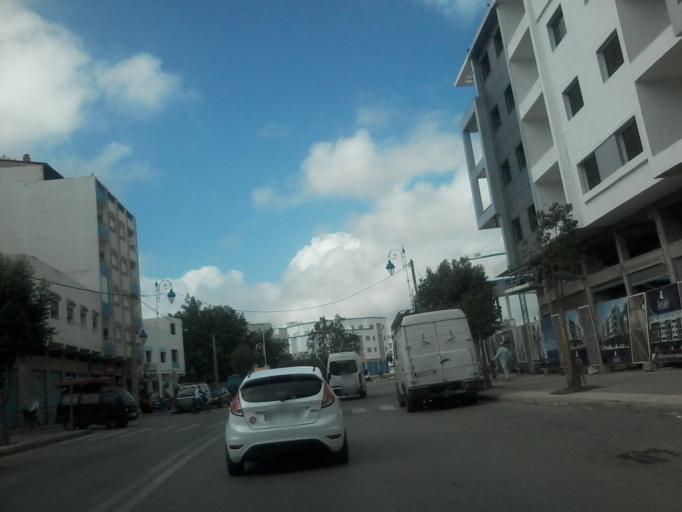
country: MA
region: Tanger-Tetouan
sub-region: Tetouan
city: Martil
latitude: 35.6270
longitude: -5.2807
